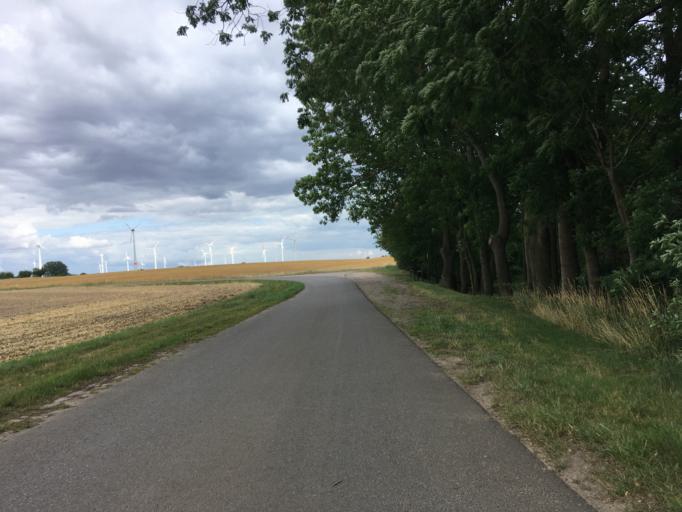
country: DE
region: Brandenburg
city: Gramzow
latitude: 53.2512
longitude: 13.9985
